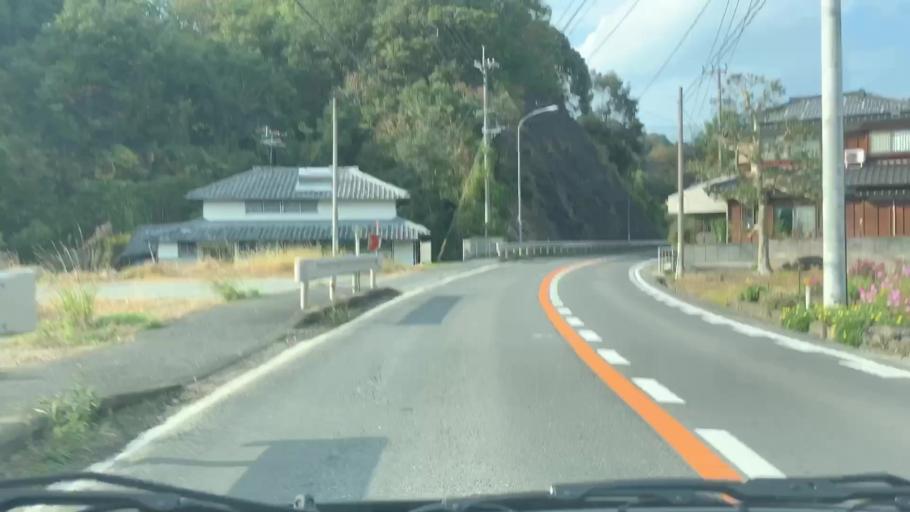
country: JP
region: Nagasaki
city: Sasebo
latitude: 32.9886
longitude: 129.7383
